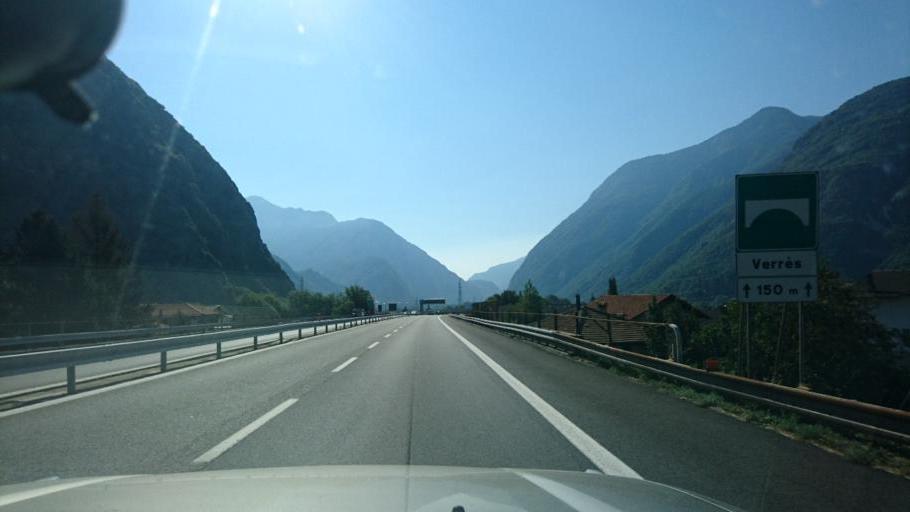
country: IT
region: Aosta Valley
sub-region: Valle d'Aosta
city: Verres
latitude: 45.6616
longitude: 7.6901
